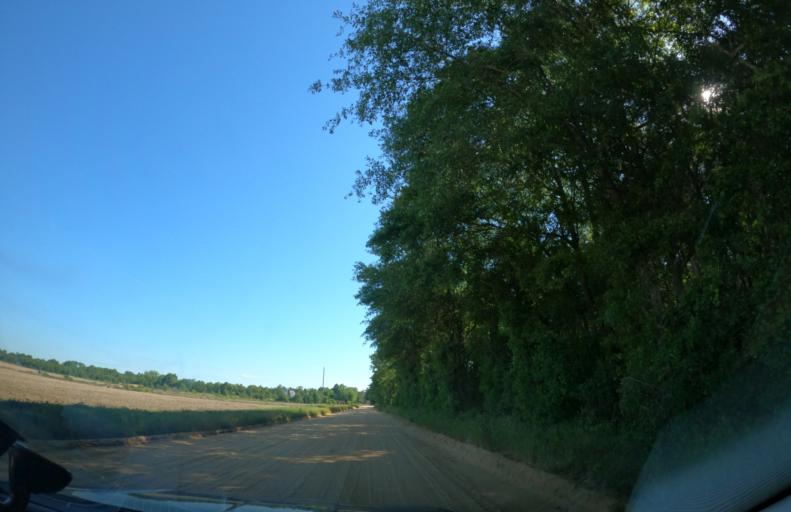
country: US
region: Georgia
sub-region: Jefferson County
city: Wrens
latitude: 33.2149
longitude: -82.3582
